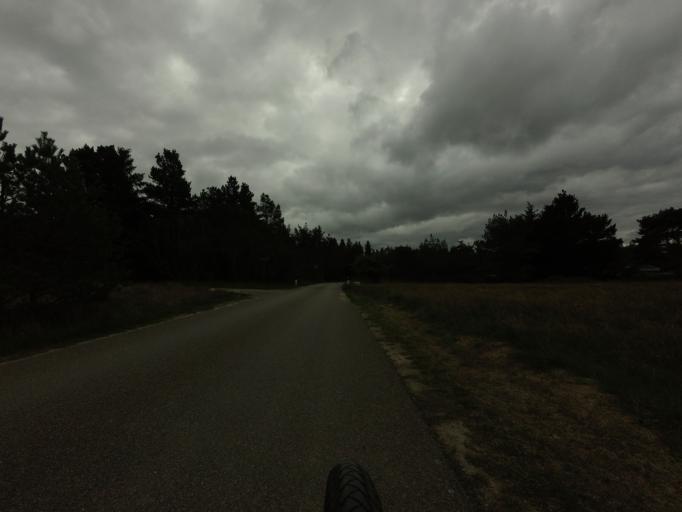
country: DK
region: North Denmark
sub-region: Hjorring Kommune
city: Sindal
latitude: 57.6121
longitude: 10.2845
